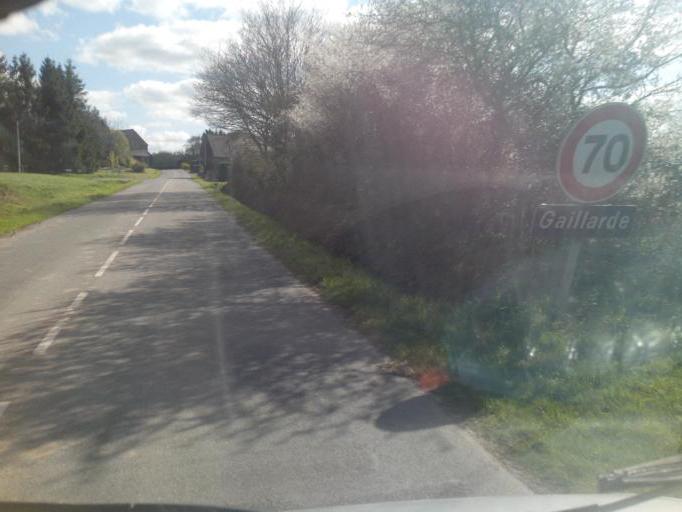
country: FR
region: Brittany
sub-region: Departement d'Ille-et-Vilaine
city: Paimpont
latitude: 48.0575
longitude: -2.1862
